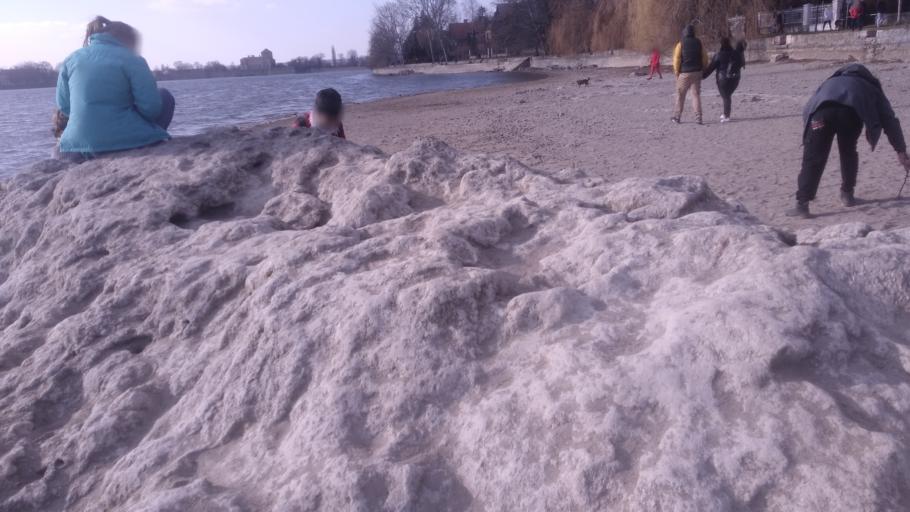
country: HU
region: Komarom-Esztergom
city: Tata
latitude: 47.6449
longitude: 18.3310
